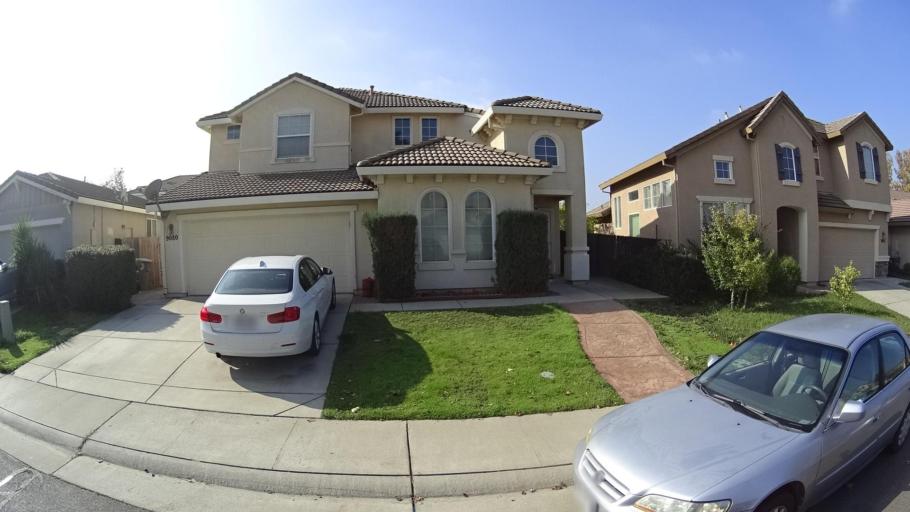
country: US
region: California
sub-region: Sacramento County
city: Vineyard
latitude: 38.4465
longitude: -121.3638
